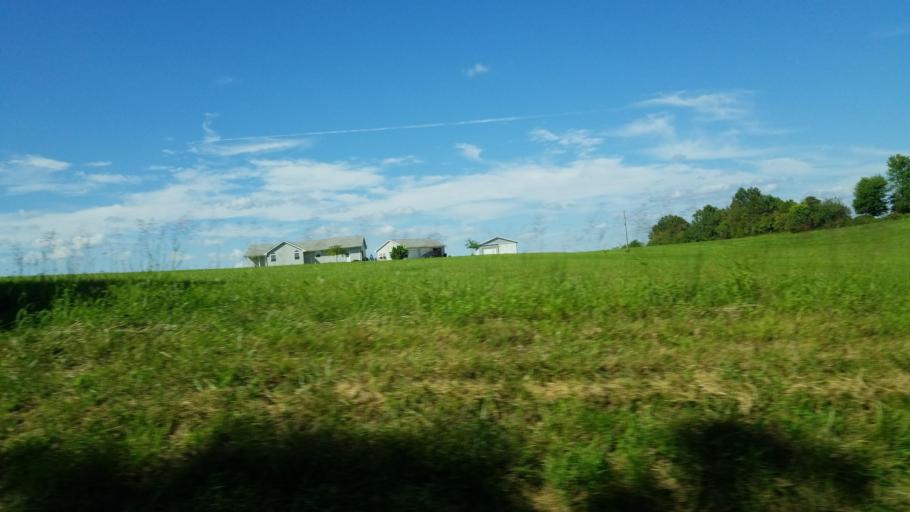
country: US
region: Illinois
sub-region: Williamson County
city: Johnston City
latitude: 37.7868
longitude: -88.7854
